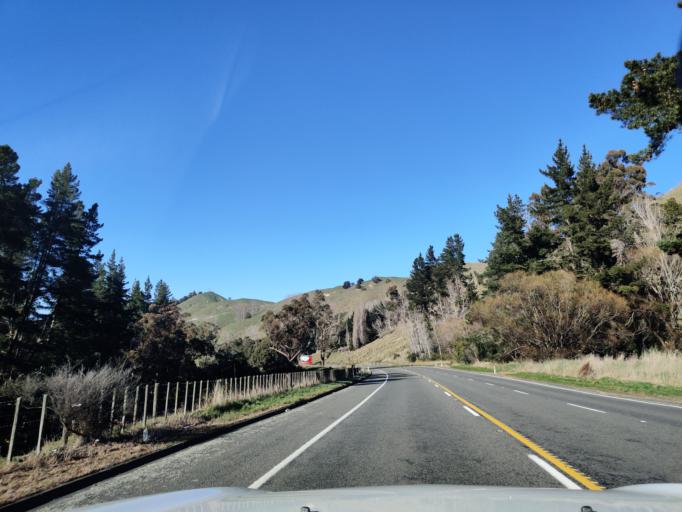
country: NZ
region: Manawatu-Wanganui
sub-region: Ruapehu District
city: Waiouru
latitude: -39.7900
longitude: 175.7851
